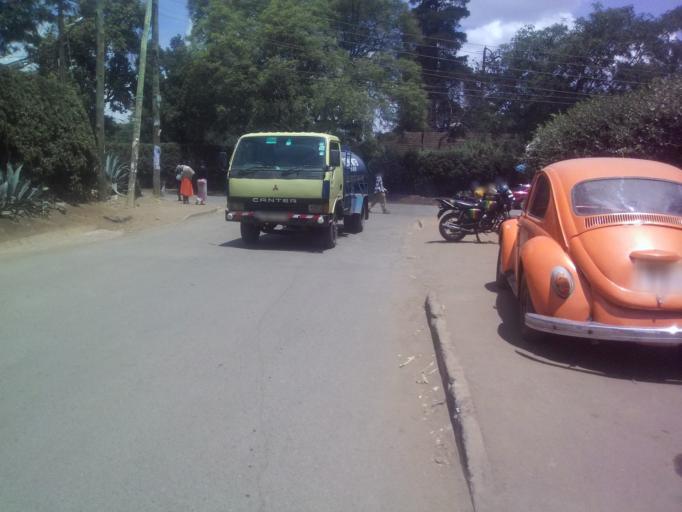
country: KE
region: Nairobi Area
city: Nairobi
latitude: -1.3041
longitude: 36.7778
